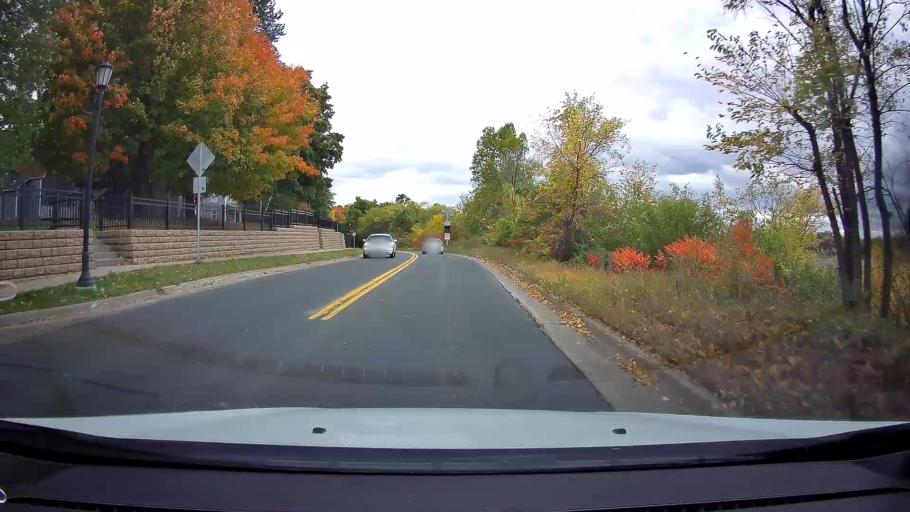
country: US
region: Minnesota
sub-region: Chisago County
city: Center City
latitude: 45.3960
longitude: -92.8185
